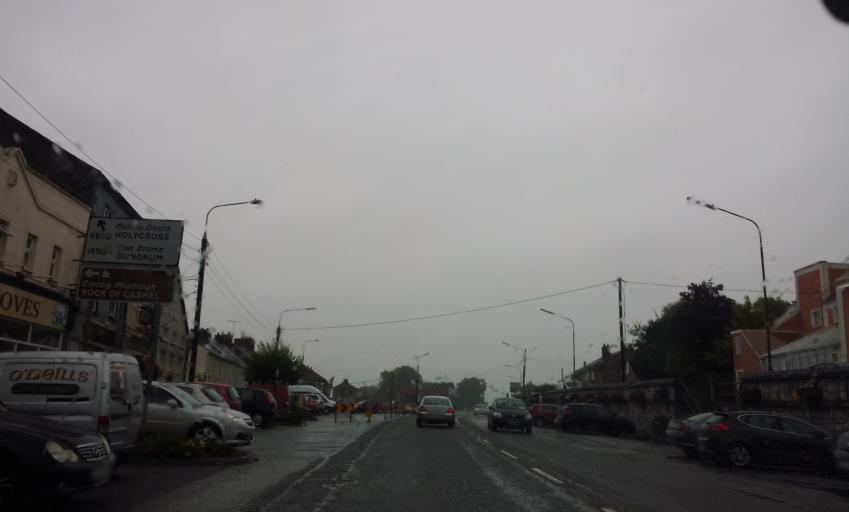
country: IE
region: Munster
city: Cashel
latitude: 52.5187
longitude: -7.8863
